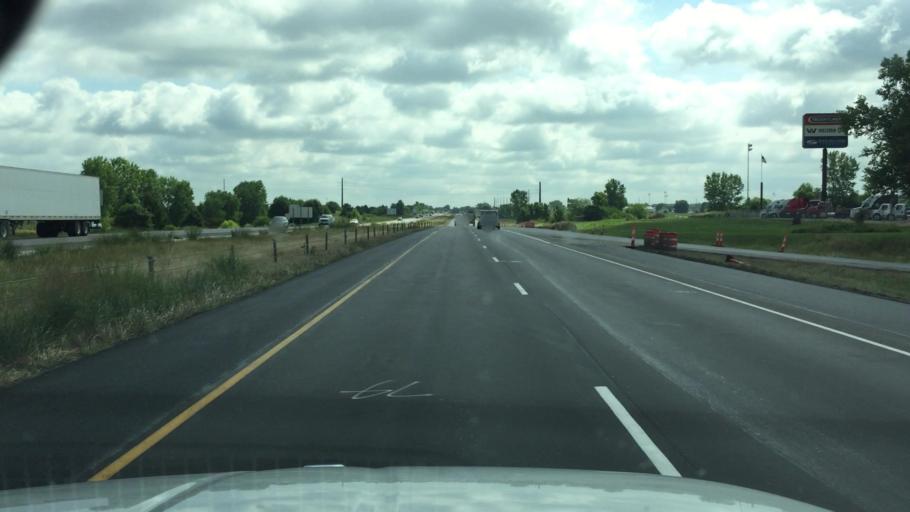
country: US
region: Iowa
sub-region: Scott County
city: Eldridge
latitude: 41.5998
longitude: -90.6146
